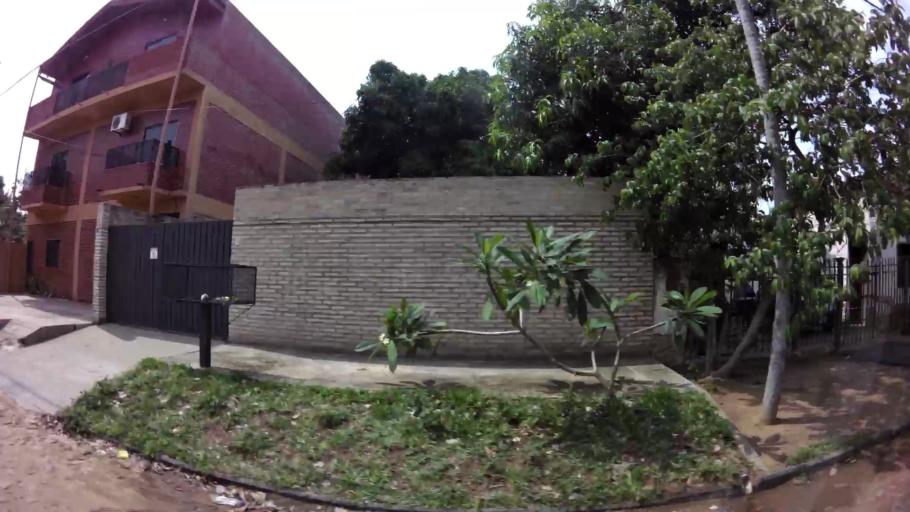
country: PY
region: Asuncion
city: Asuncion
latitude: -25.2615
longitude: -57.5855
